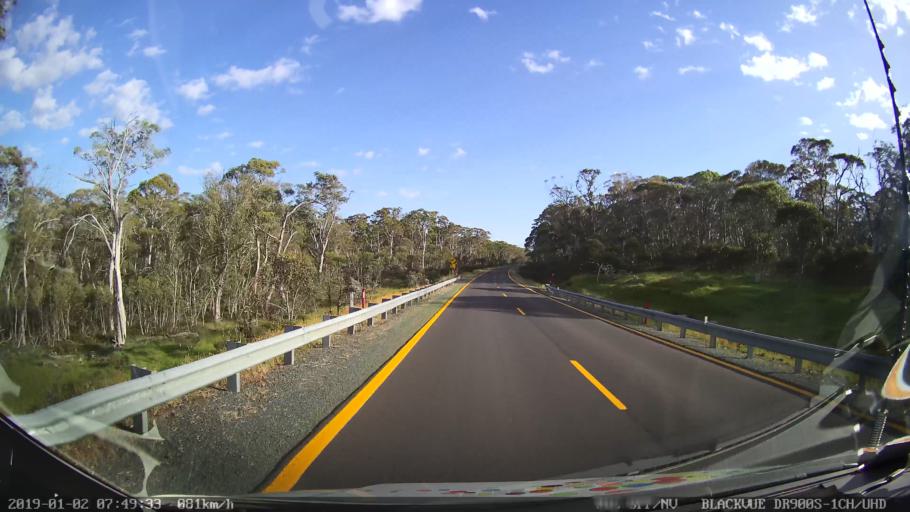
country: AU
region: New South Wales
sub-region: Tumut Shire
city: Tumut
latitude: -35.7403
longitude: 148.5226
